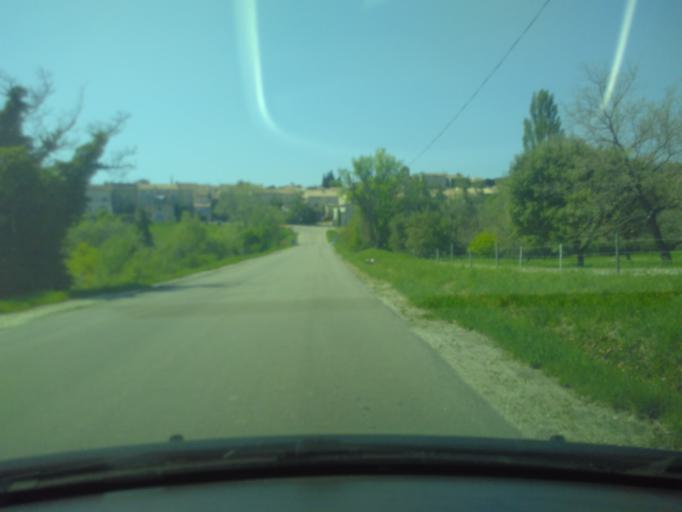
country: FR
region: Rhone-Alpes
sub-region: Departement de la Drome
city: Grignan
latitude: 44.4510
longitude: 4.9373
